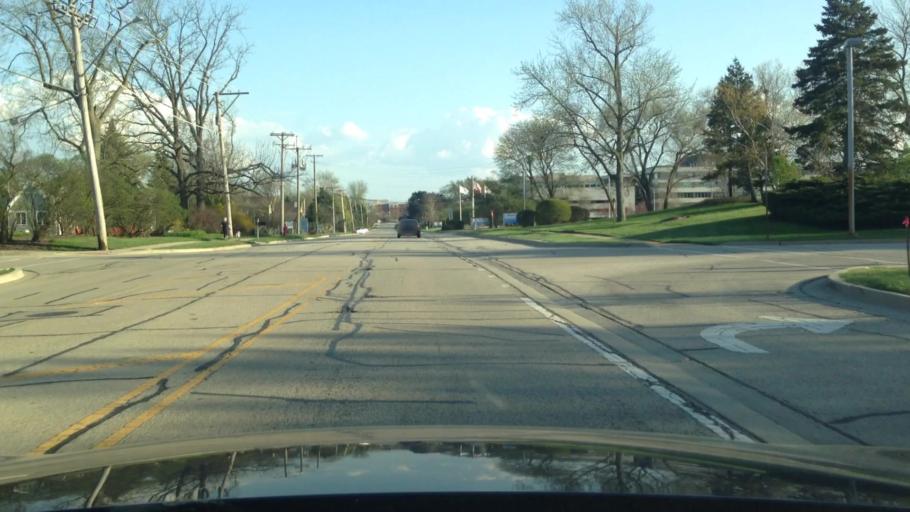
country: US
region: Illinois
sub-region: Lake County
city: Deerfield
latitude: 42.1587
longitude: -87.8674
